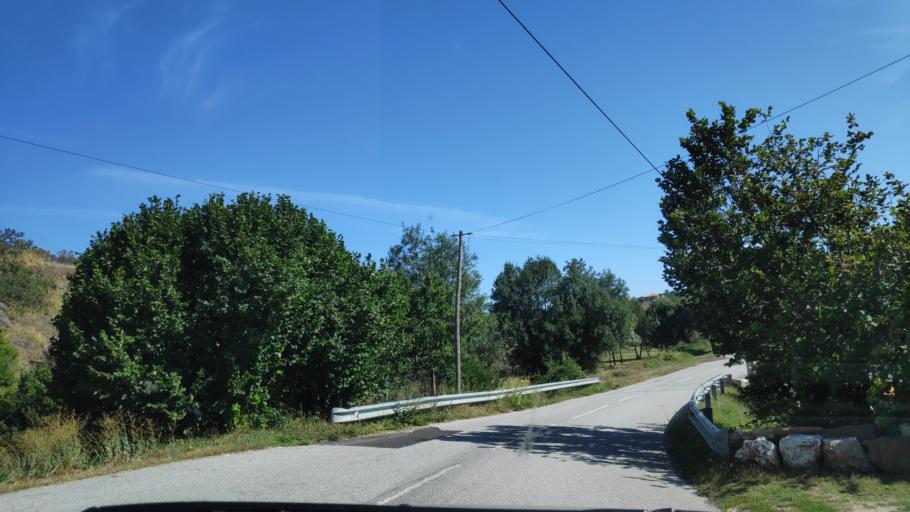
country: ES
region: Castille and Leon
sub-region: Provincia de Zamora
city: Alcanices
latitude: 41.6305
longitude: -6.3532
